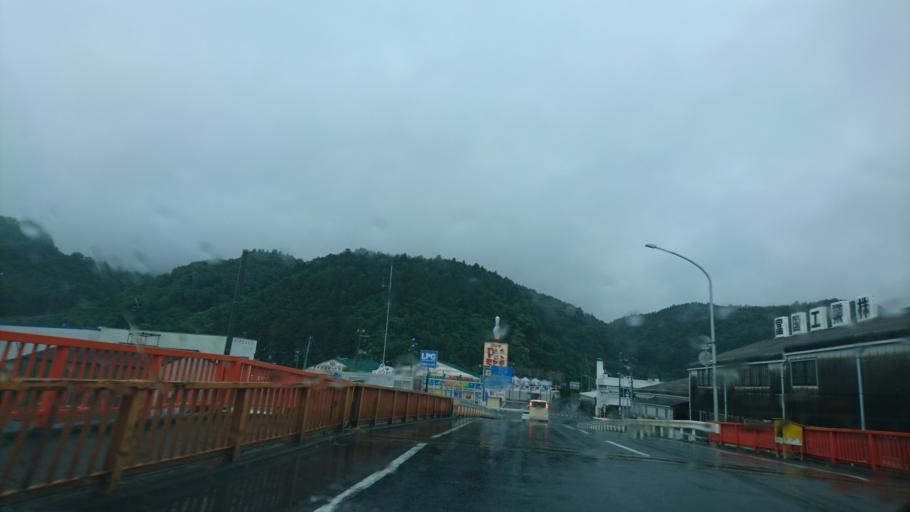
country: JP
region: Miyagi
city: Ishinomaki
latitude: 38.4373
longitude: 141.3176
